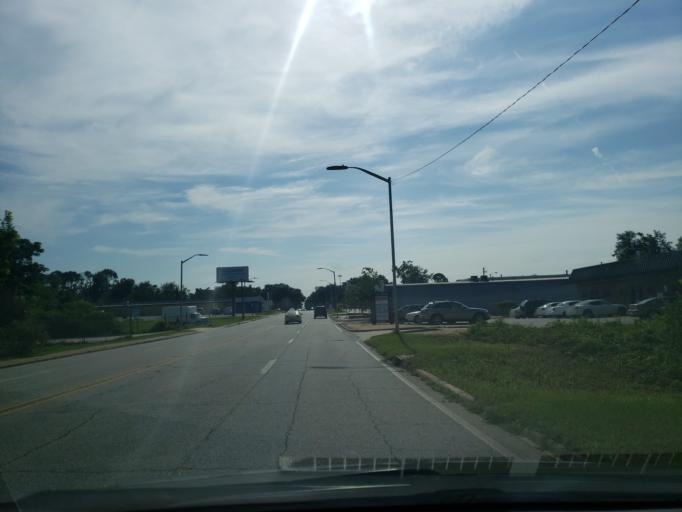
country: US
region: Georgia
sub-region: Dougherty County
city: Albany
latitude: 31.5785
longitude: -84.1677
